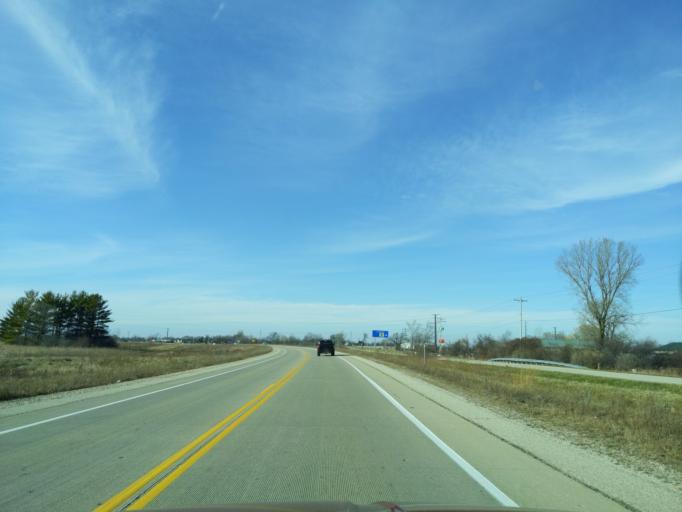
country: US
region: Wisconsin
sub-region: Walworth County
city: Whitewater
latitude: 42.8168
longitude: -88.6933
